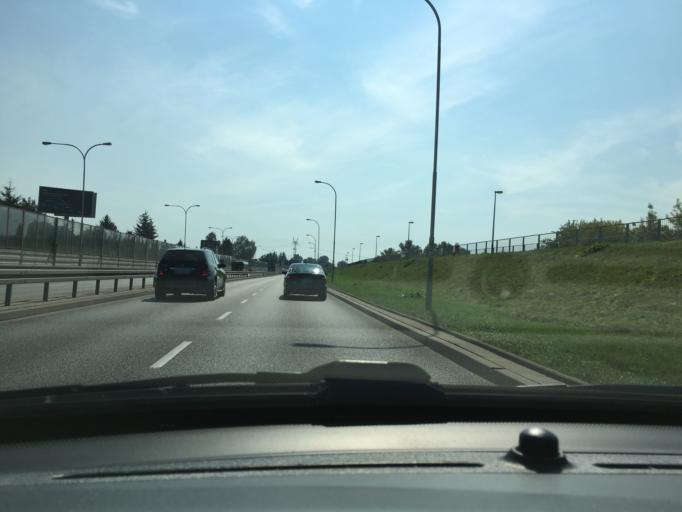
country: PL
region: Masovian Voivodeship
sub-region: Warszawa
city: Praga Poludnie
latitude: 52.2068
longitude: 21.1110
